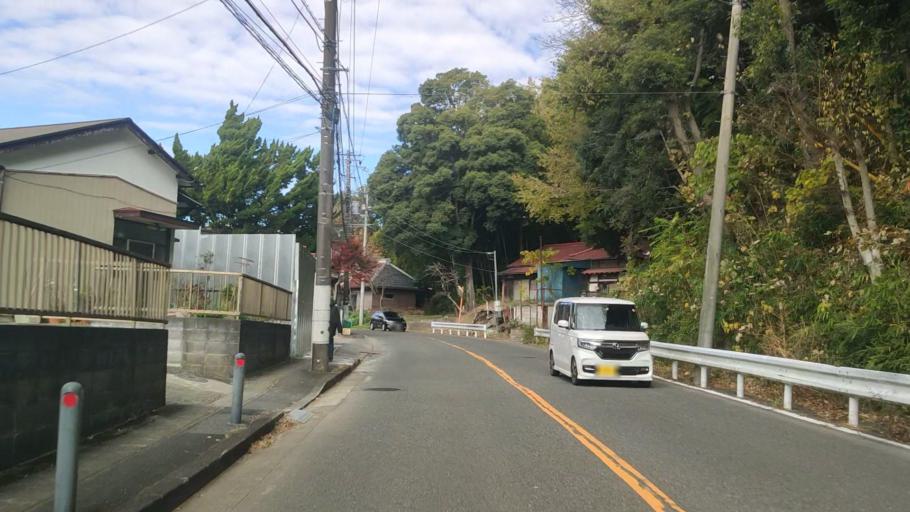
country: JP
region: Kanagawa
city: Yokohama
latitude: 35.4371
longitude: 139.5448
